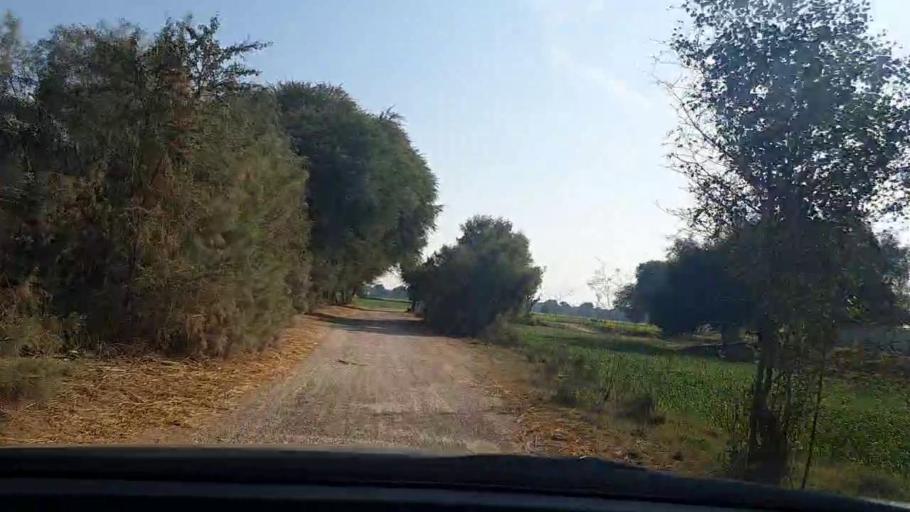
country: PK
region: Sindh
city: Sehwan
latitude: 26.3053
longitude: 68.0016
